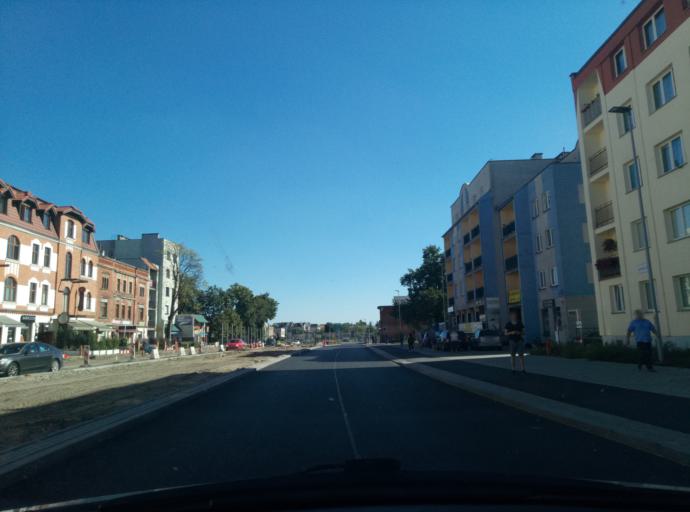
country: PL
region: Kujawsko-Pomorskie
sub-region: Torun
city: Torun
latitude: 53.0277
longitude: 18.5910
